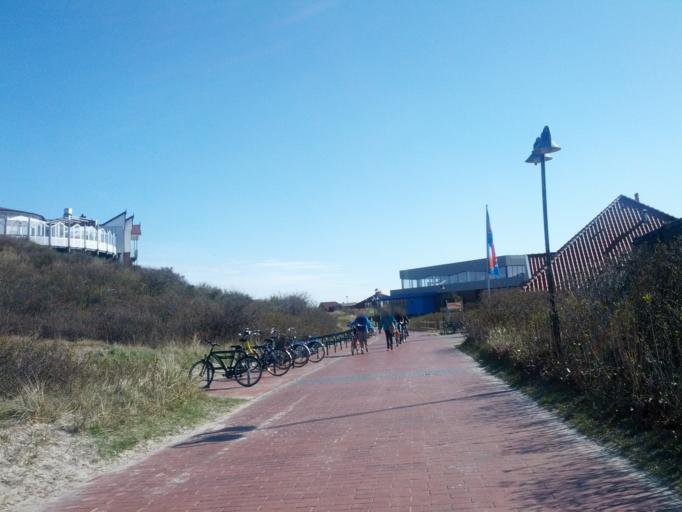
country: DE
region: Lower Saxony
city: Langeoog
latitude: 53.7502
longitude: 7.4764
